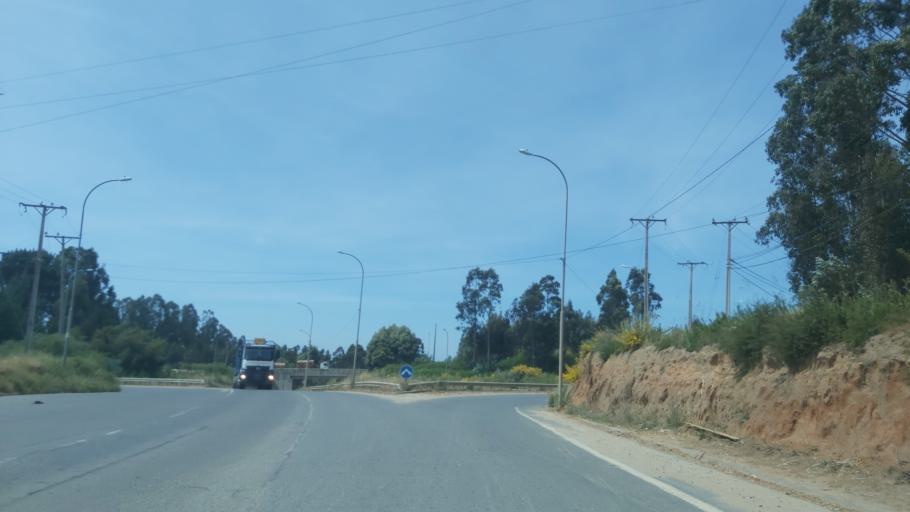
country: CL
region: Maule
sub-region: Provincia de Talca
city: Constitucion
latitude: -35.3672
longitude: -72.4025
